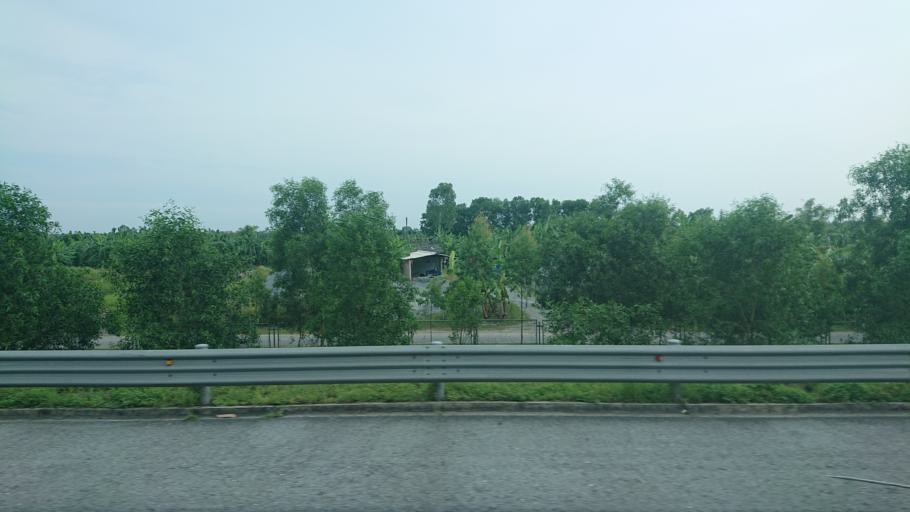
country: VN
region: Hai Duong
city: Tu Ky
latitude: 20.8231
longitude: 106.4700
